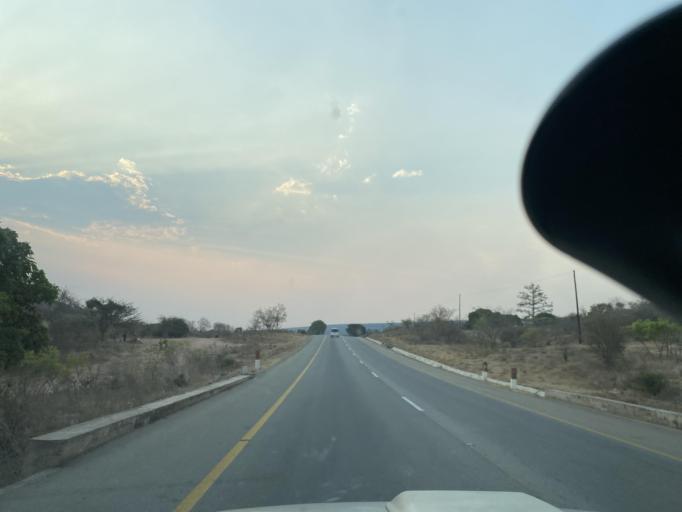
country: ZM
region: Lusaka
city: Kafue
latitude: -15.9050
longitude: 28.3497
